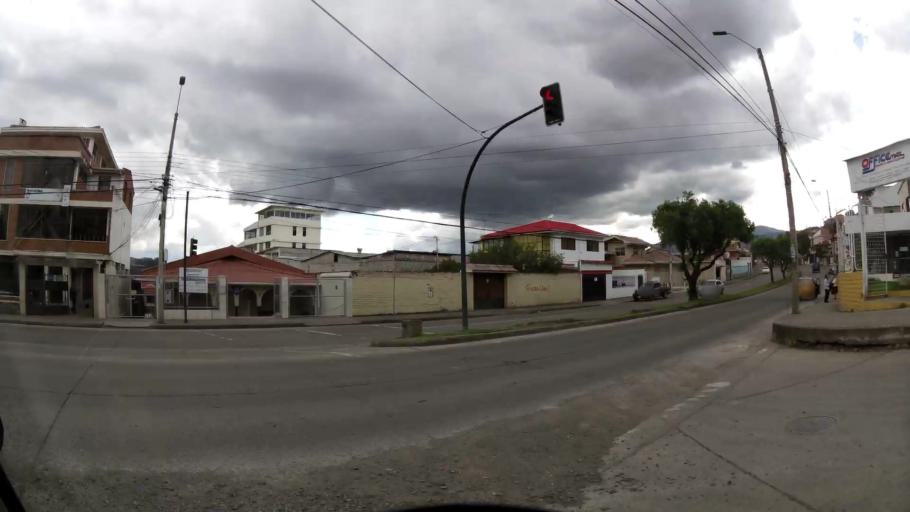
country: EC
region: Azuay
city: Cuenca
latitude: -2.8876
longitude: -79.0077
